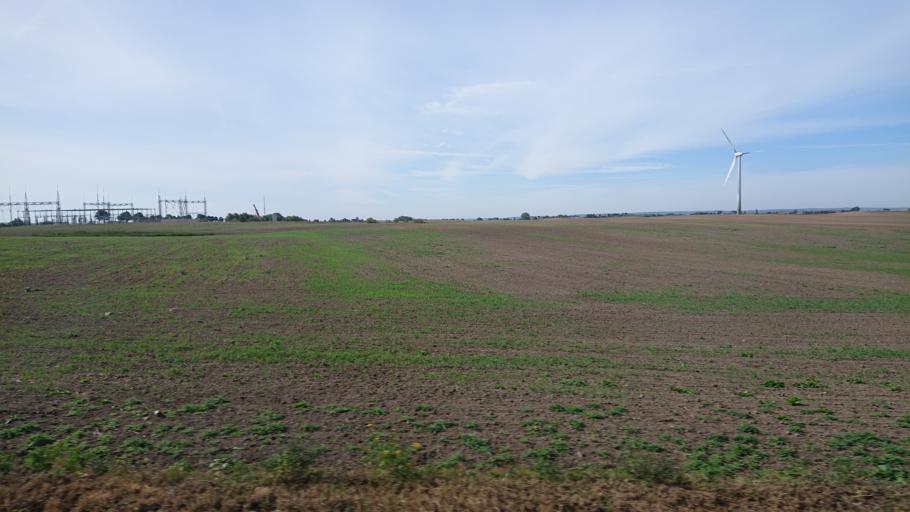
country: DE
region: Brandenburg
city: Grunow
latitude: 53.2559
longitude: 13.9605
